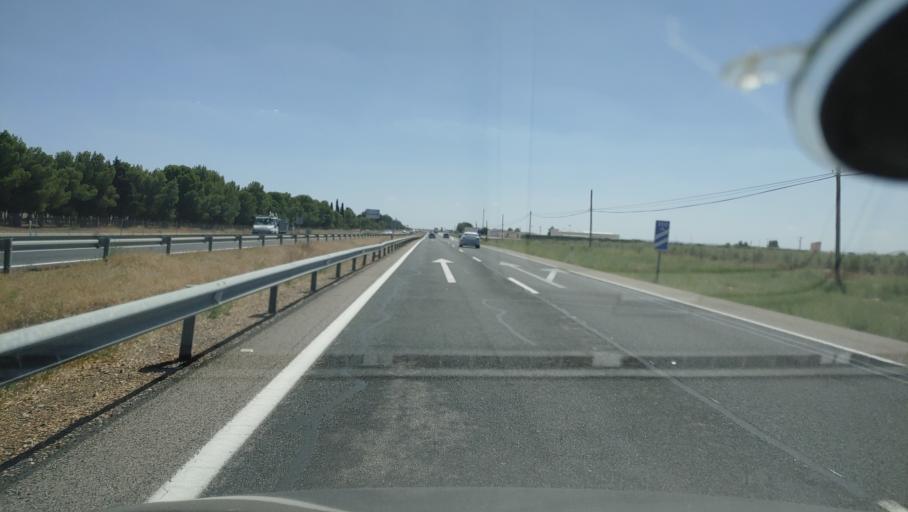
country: ES
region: Castille-La Mancha
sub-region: Provincia de Ciudad Real
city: Manzanares
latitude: 39.1180
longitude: -3.3776
